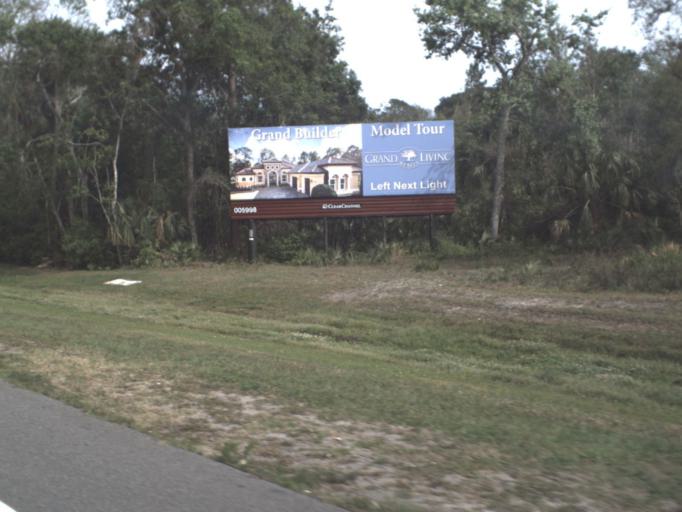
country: US
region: Florida
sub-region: Flagler County
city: Flagler Beach
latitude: 29.4760
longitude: -81.1765
